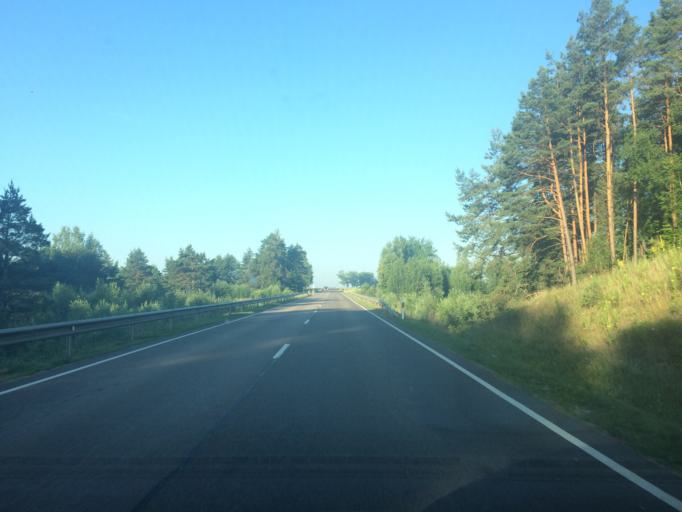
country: LT
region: Utenos apskritis
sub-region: Anyksciai
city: Anyksciai
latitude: 55.4077
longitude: 25.1932
